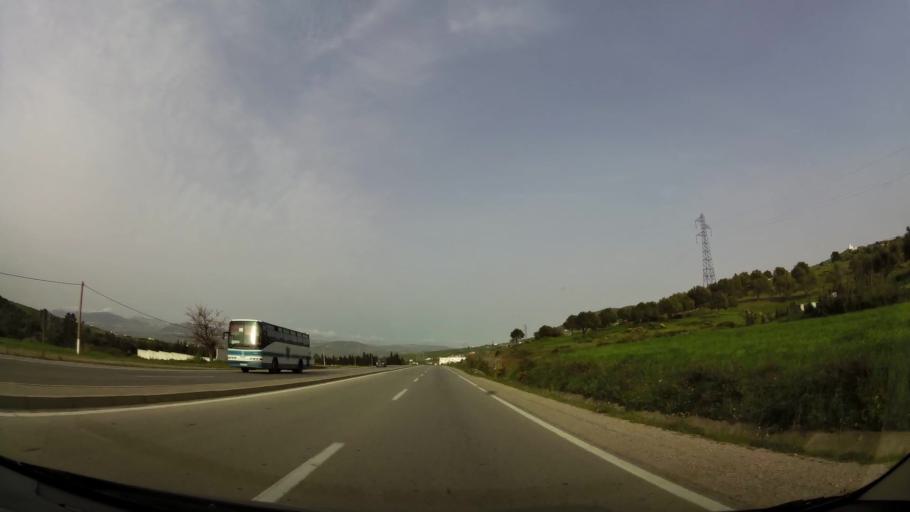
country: MA
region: Tanger-Tetouan
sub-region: Tetouan
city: Saddina
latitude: 35.5508
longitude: -5.5178
